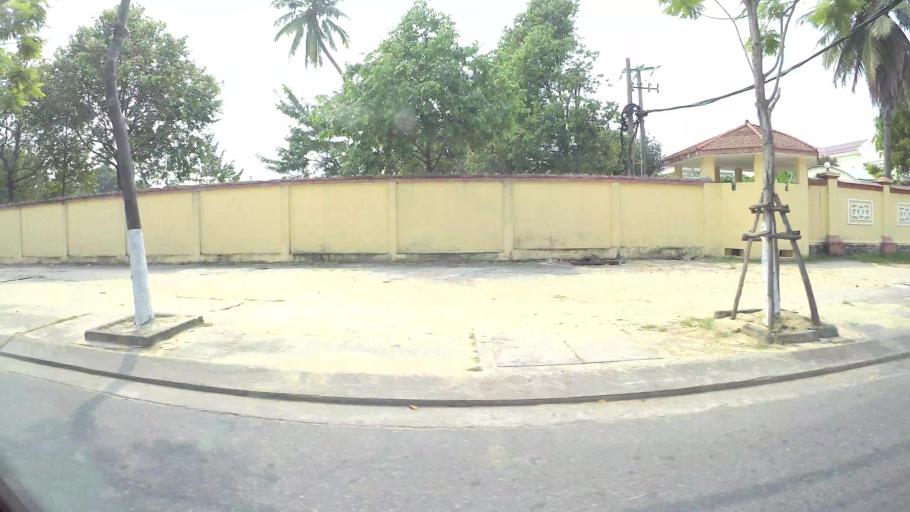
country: VN
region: Da Nang
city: Son Tra
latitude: 16.0473
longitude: 108.2210
